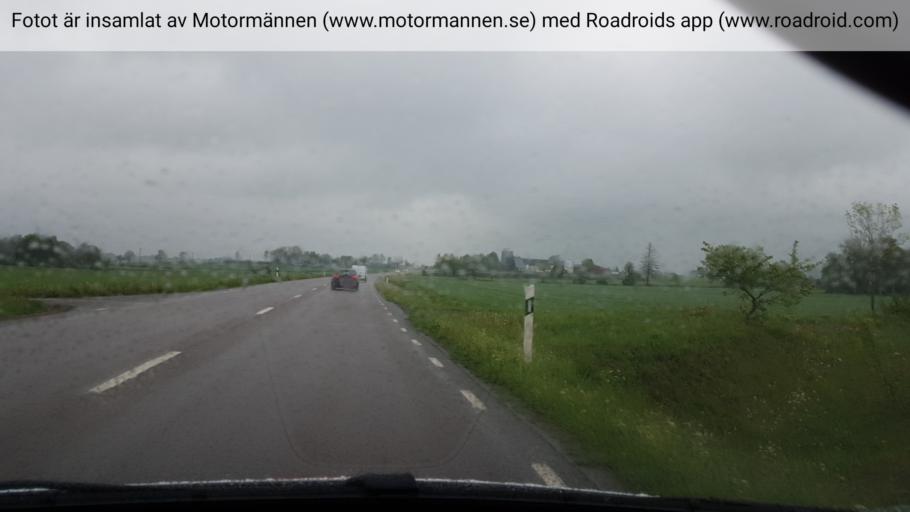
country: SE
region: Vaestra Goetaland
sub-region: Falkopings Kommun
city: Falkoeping
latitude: 58.1194
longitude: 13.5454
